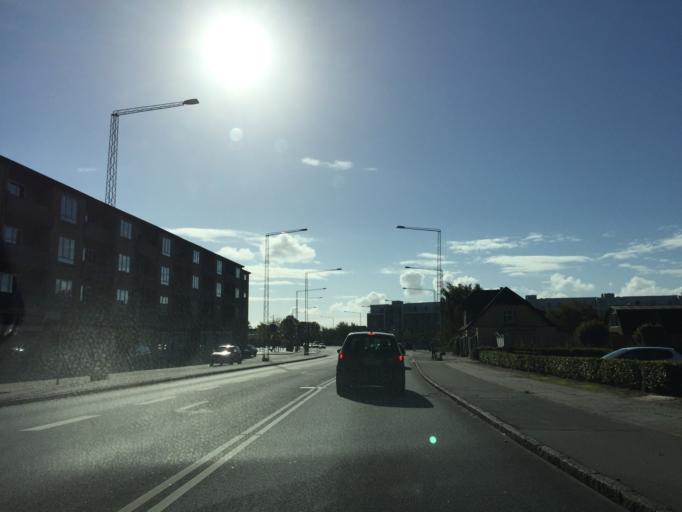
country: DK
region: Central Jutland
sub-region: Arhus Kommune
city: Arhus
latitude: 56.1684
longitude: 10.1621
